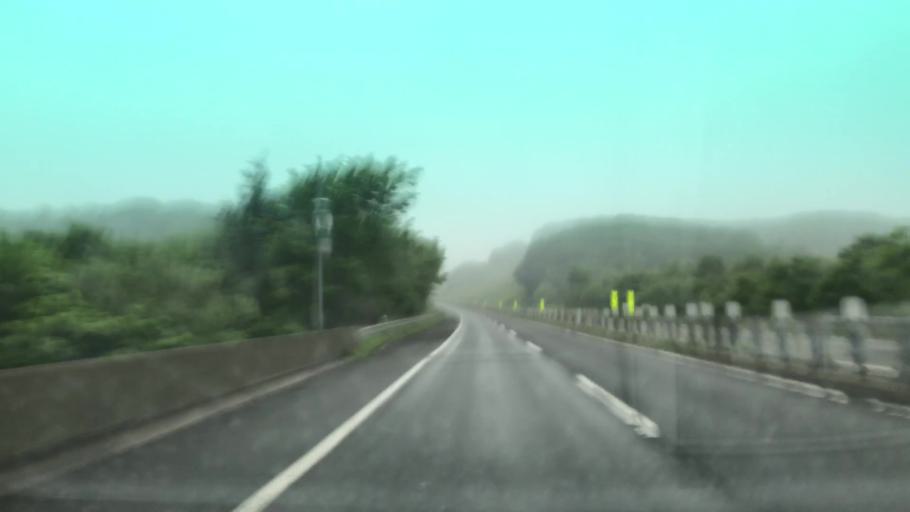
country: JP
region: Hokkaido
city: Tomakomai
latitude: 42.6511
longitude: 141.5480
